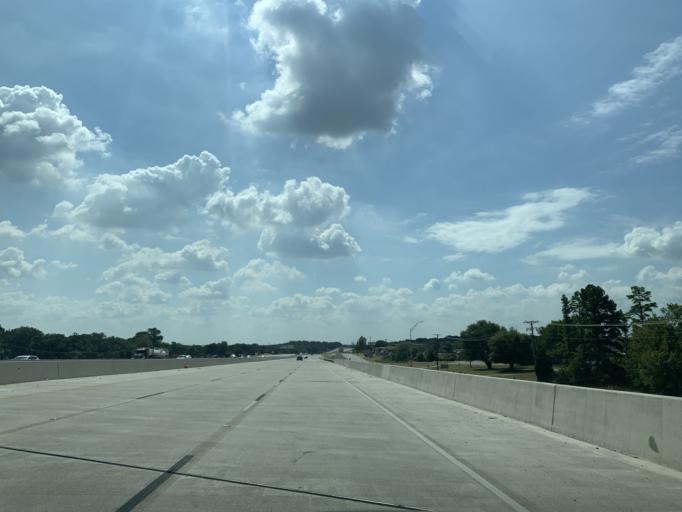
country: US
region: Texas
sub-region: Tarrant County
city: Lakeside
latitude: 32.8551
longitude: -97.5120
